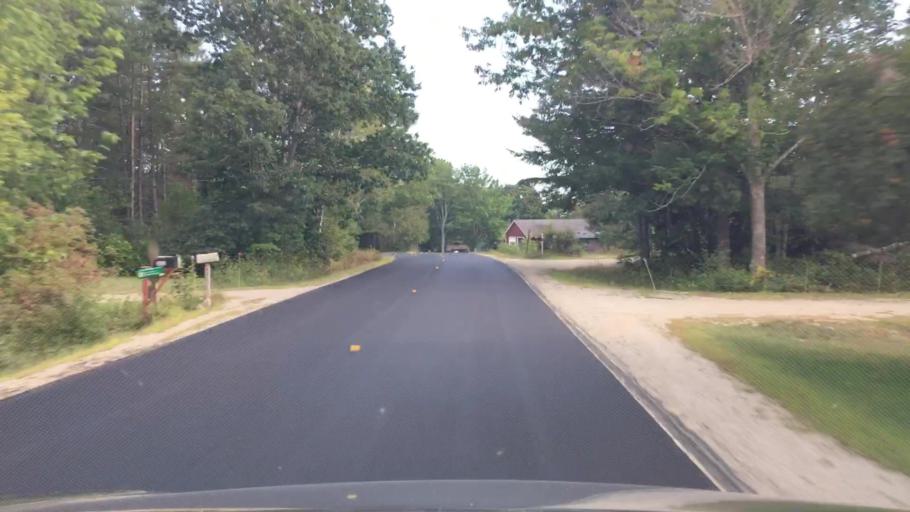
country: US
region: Maine
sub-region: Hancock County
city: Orland
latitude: 44.5466
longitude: -68.6203
